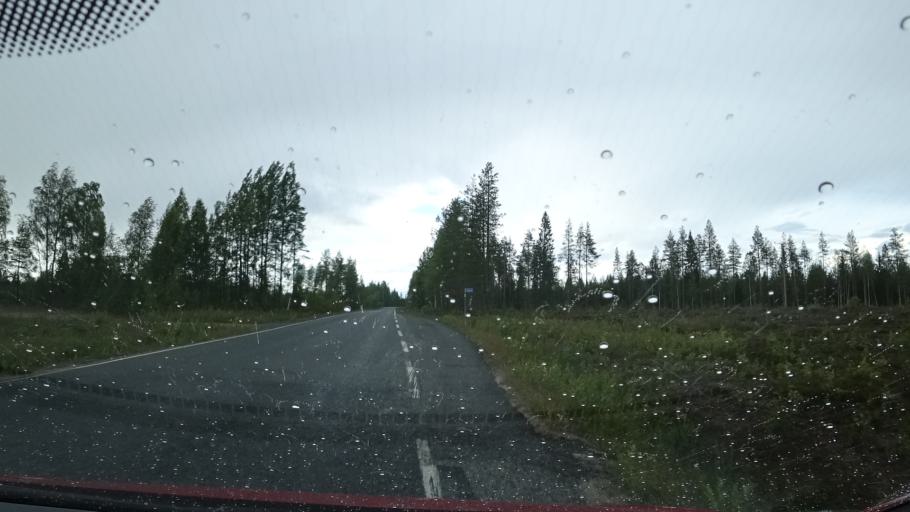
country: FI
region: Kainuu
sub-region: Kehys-Kainuu
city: Kuhmo
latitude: 63.9798
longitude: 29.2627
